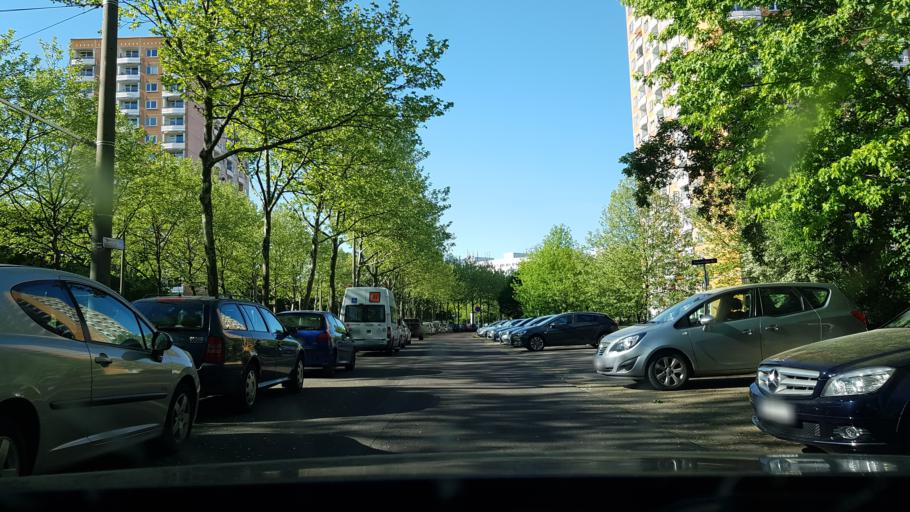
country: DE
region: Saxony
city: Kreischa
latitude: 51.0030
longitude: 13.7983
